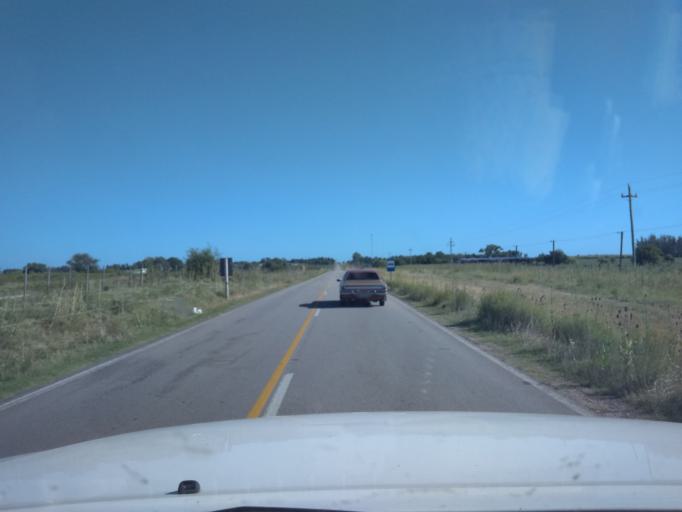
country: UY
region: Canelones
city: San Ramon
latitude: -34.3182
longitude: -55.9595
